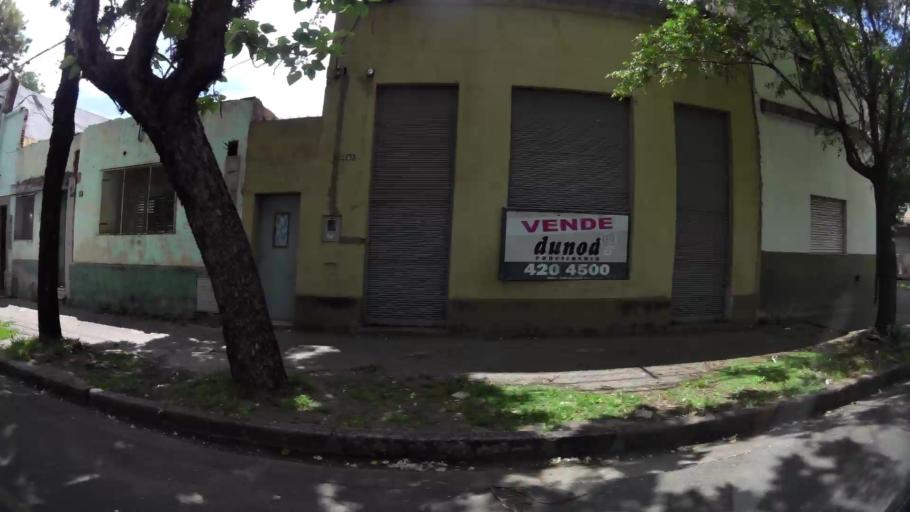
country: AR
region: Santa Fe
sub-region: Departamento de Rosario
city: Rosario
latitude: -32.9721
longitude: -60.6343
